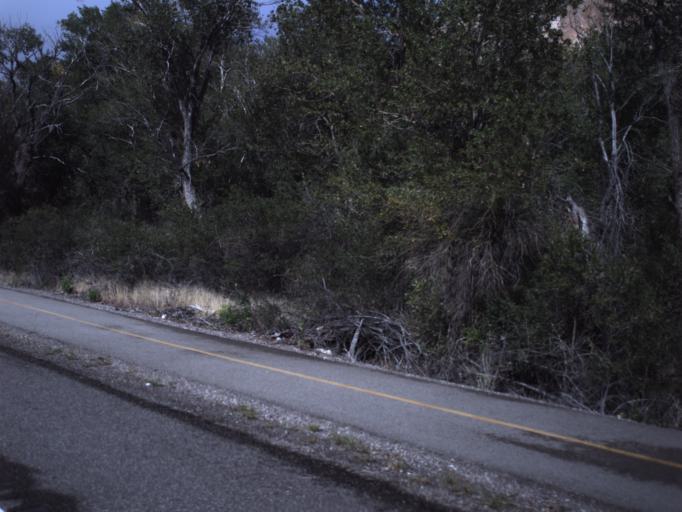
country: US
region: Utah
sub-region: Sevier County
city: Monroe
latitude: 38.5767
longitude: -112.2582
